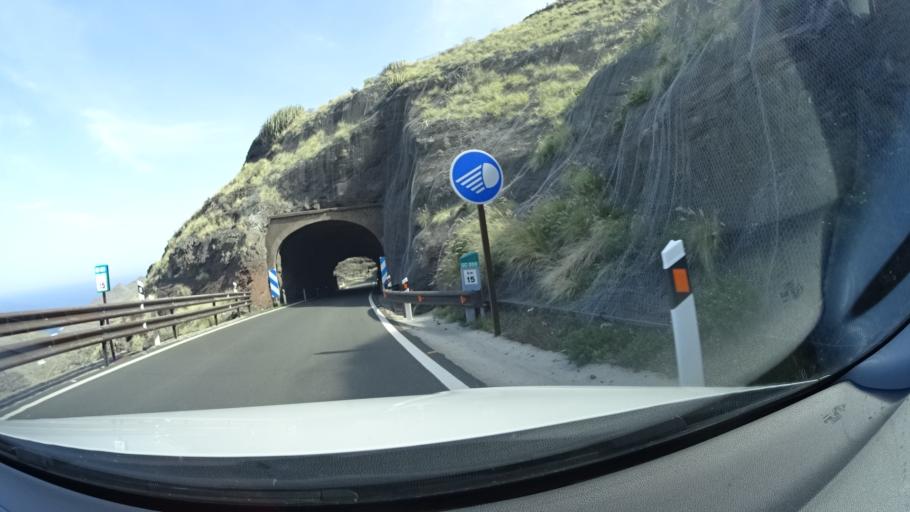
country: ES
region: Canary Islands
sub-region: Provincia de Las Palmas
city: San Nicolas
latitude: 28.0409
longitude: -15.7356
